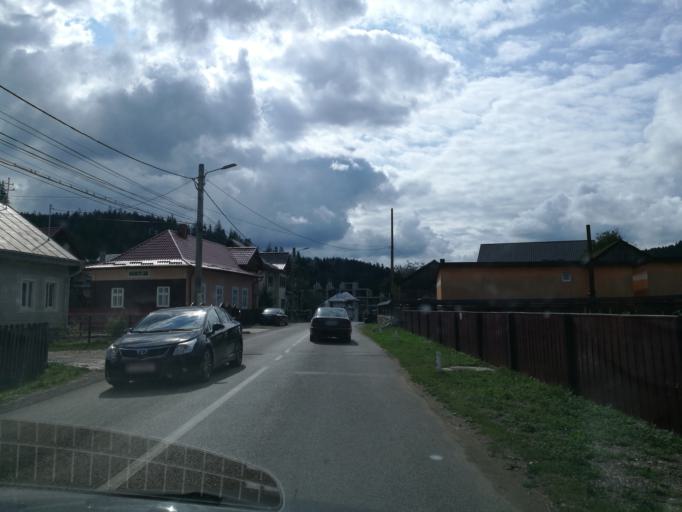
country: RO
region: Suceava
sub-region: Oras Gura Humorului
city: Gura Humorului
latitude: 47.5226
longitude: 25.8644
